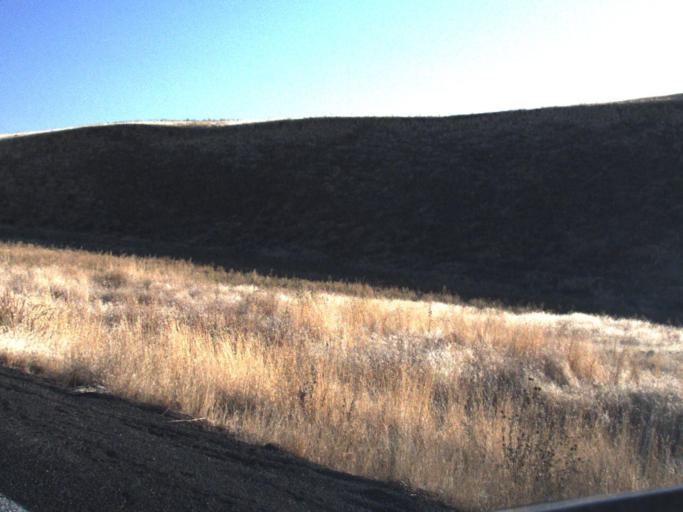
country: US
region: Washington
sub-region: Adams County
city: Ritzville
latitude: 46.8096
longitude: -118.3094
